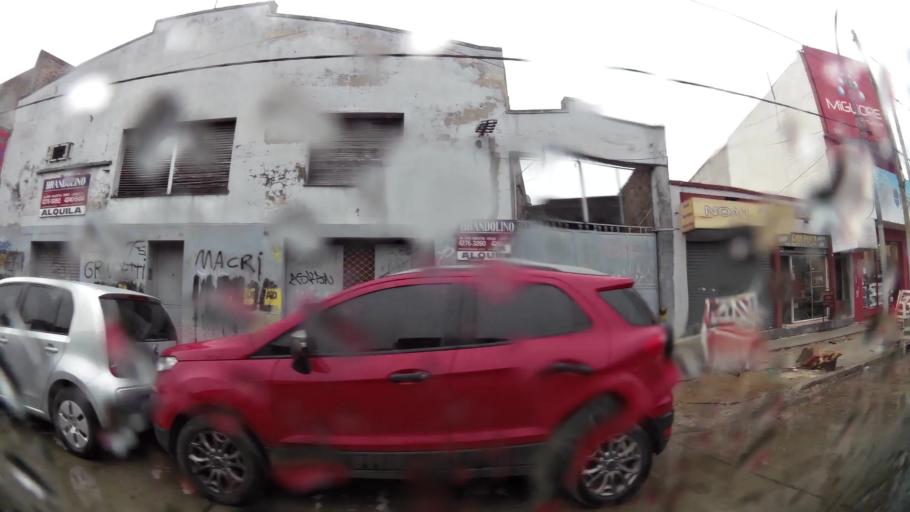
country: AR
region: Buenos Aires
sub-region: Partido de Lanus
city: Lanus
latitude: -34.7047
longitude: -58.4159
